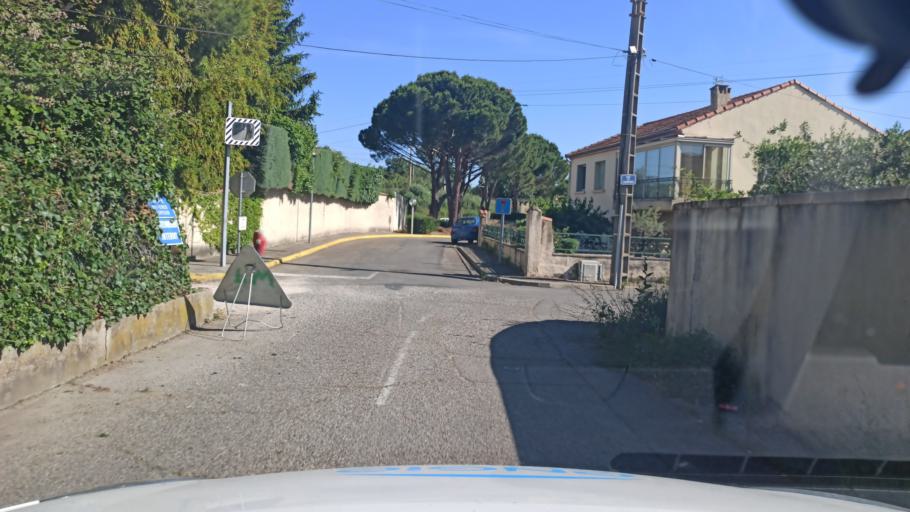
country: FR
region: Provence-Alpes-Cote d'Azur
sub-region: Departement du Vaucluse
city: Le Pontet
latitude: 43.9581
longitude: 4.8479
